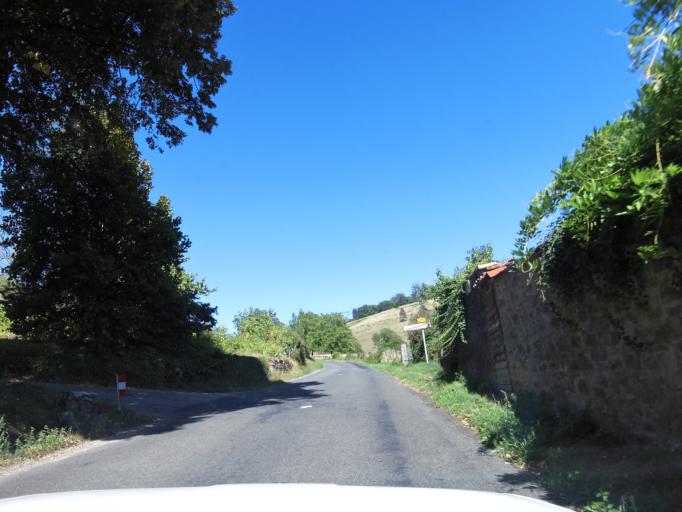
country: FR
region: Rhone-Alpes
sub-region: Departement de l'Ain
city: Vaux-en-Bugey
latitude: 45.9306
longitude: 5.3551
